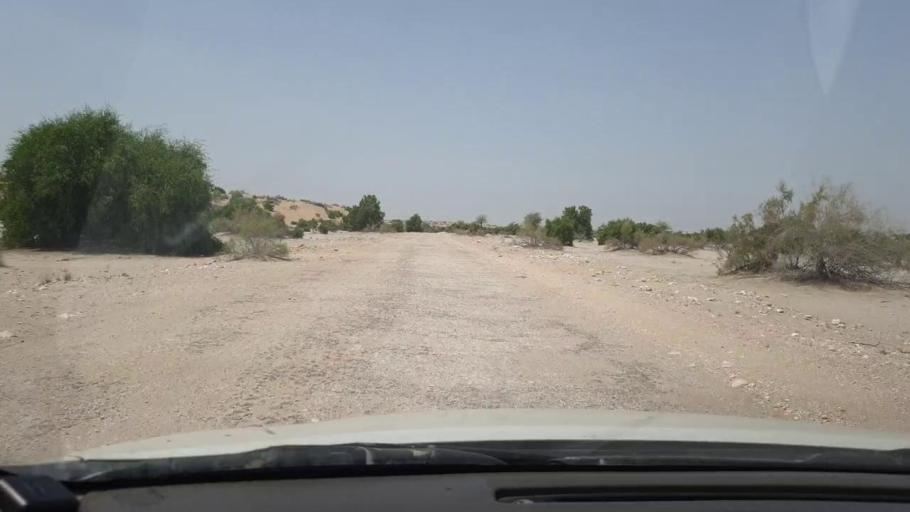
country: PK
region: Sindh
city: Rohri
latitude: 27.2958
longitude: 69.2715
